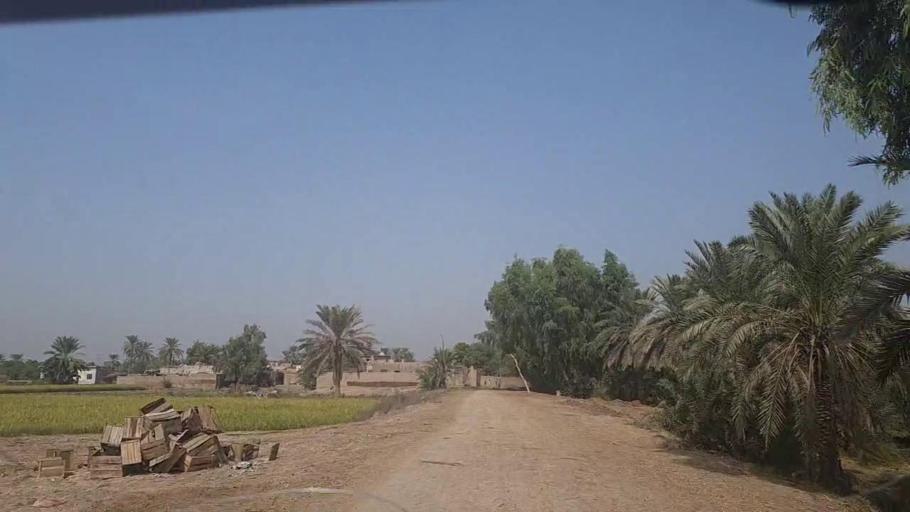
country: PK
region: Sindh
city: Madeji
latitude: 27.8059
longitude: 68.4265
